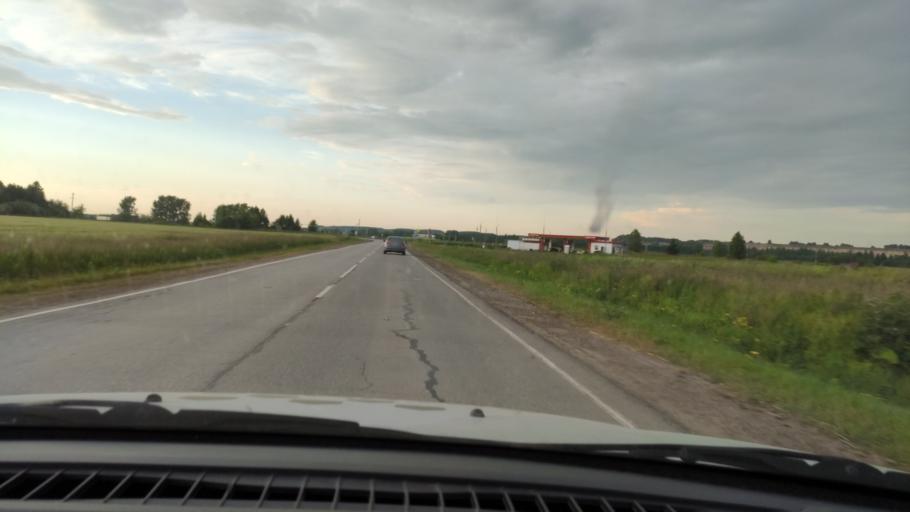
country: RU
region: Perm
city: Kukushtan
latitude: 57.5006
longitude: 56.6473
